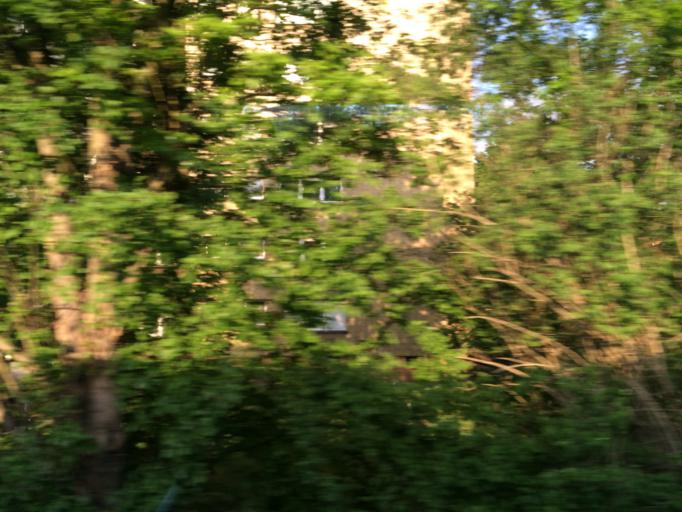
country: DE
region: North Rhine-Westphalia
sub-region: Regierungsbezirk Dusseldorf
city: Hochfeld
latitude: 51.4084
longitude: 6.7726
